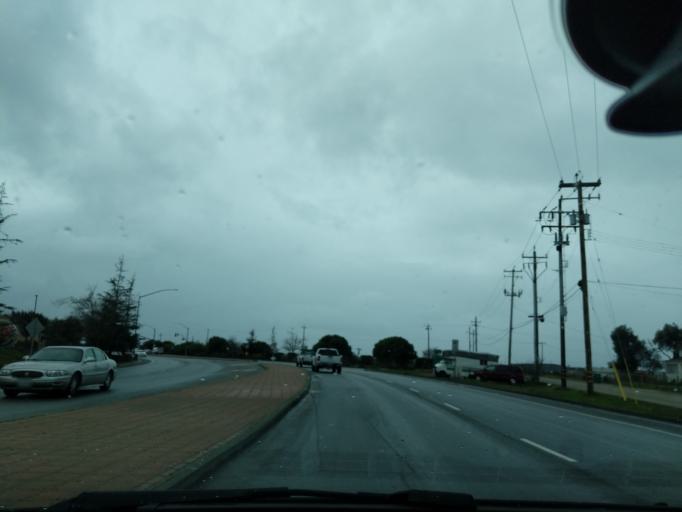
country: US
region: California
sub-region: Monterey County
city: Boronda
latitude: 36.7223
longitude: -121.6630
